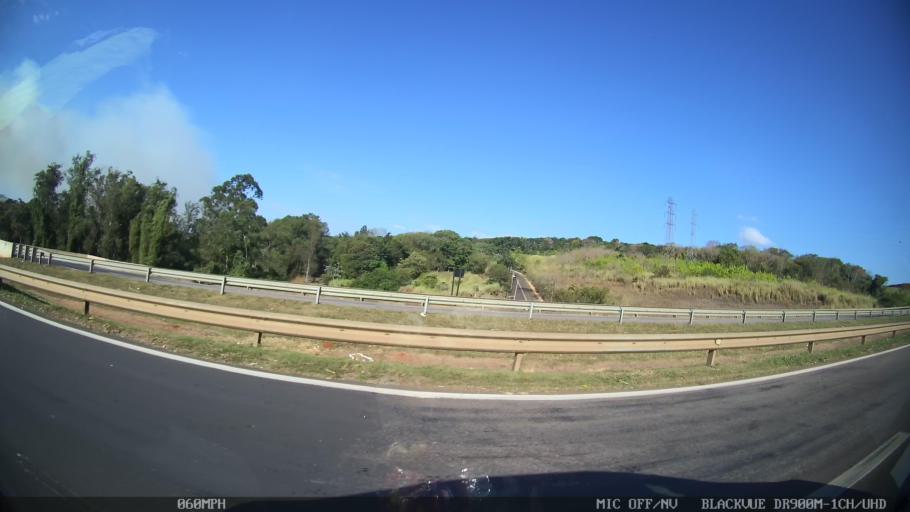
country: BR
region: Sao Paulo
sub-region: Piracicaba
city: Piracicaba
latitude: -22.7018
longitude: -47.6101
